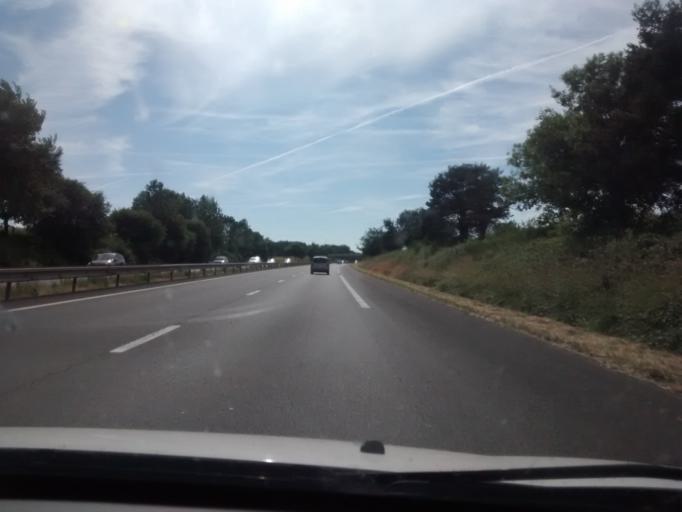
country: FR
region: Pays de la Loire
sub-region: Departement de la Sarthe
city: Trange
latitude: 48.0376
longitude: 0.0595
